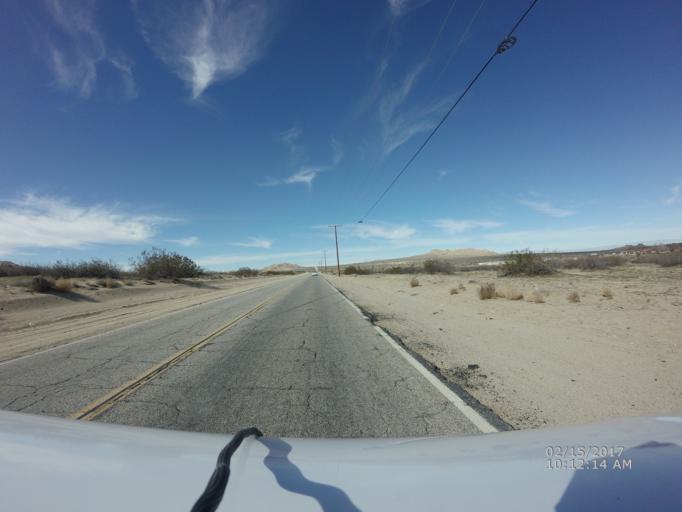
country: US
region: California
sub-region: Los Angeles County
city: Lake Los Angeles
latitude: 34.6165
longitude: -117.8583
